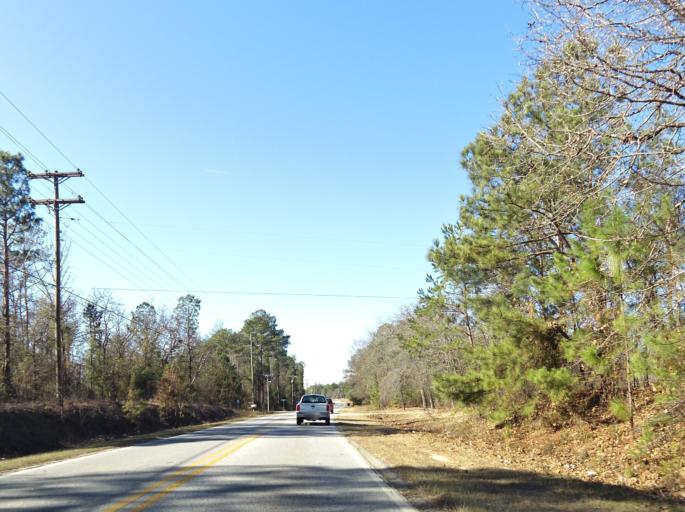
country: US
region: Georgia
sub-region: Bibb County
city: West Point
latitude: 32.7563
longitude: -83.7516
